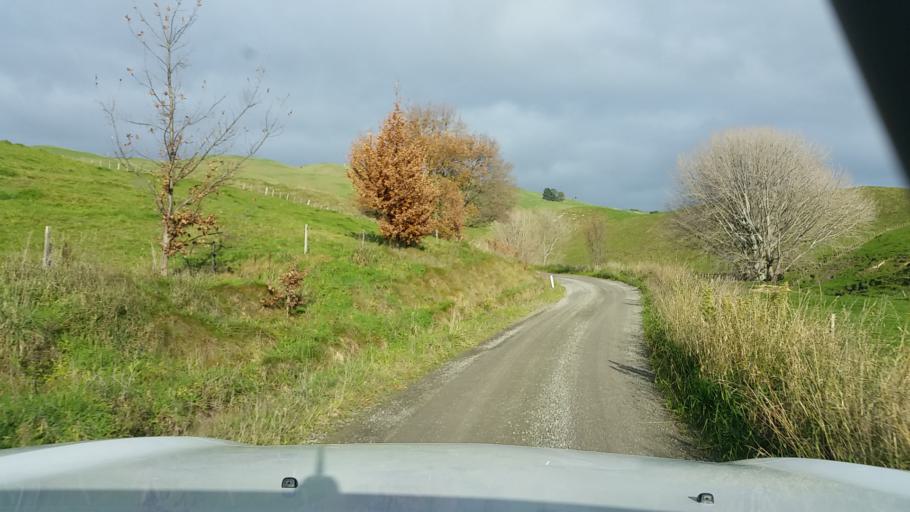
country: NZ
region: Wellington
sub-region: Masterton District
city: Masterton
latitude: -41.0333
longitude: 175.7037
